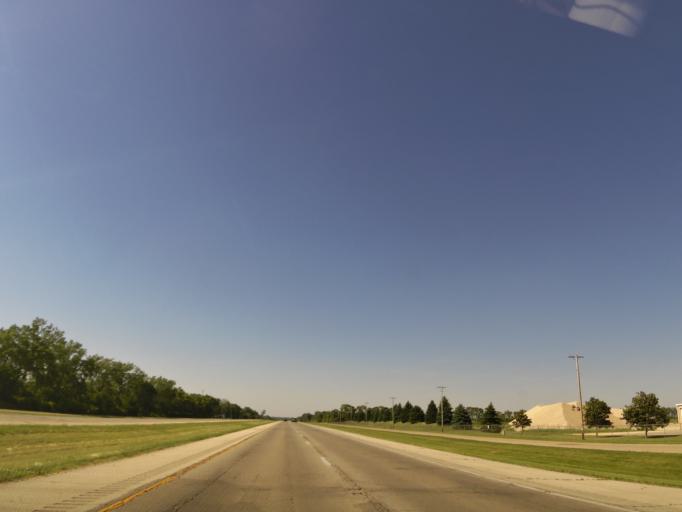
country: US
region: Illinois
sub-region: Winnebago County
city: South Beloit
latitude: 42.4742
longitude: -89.0195
